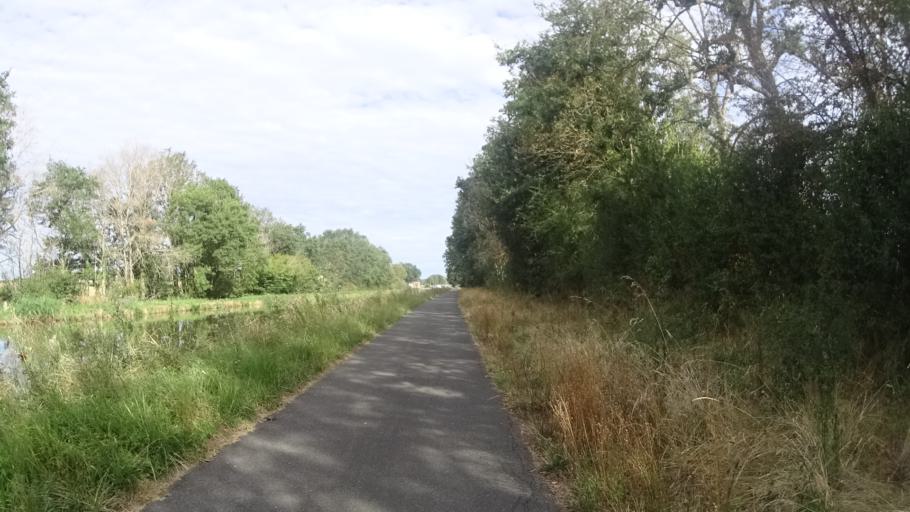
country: FR
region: Auvergne
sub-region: Departement de l'Allier
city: Diou
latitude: 46.5217
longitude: 3.7794
